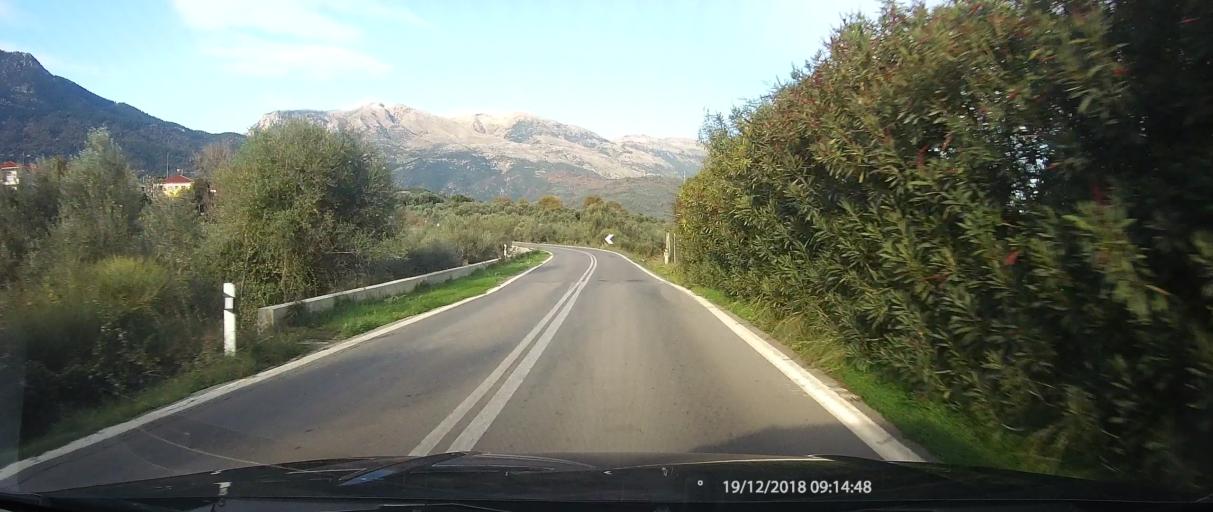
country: GR
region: Peloponnese
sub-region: Nomos Lakonias
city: Magoula
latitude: 37.0886
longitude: 22.3843
